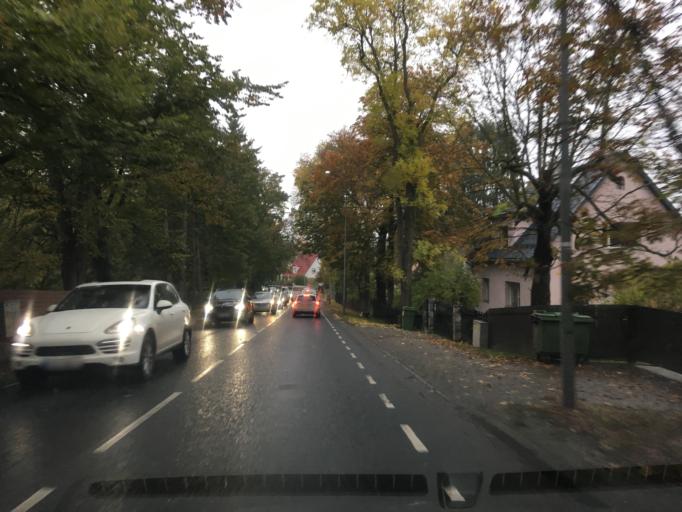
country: EE
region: Harju
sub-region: Tallinna linn
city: Kose
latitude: 59.4557
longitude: 24.8695
